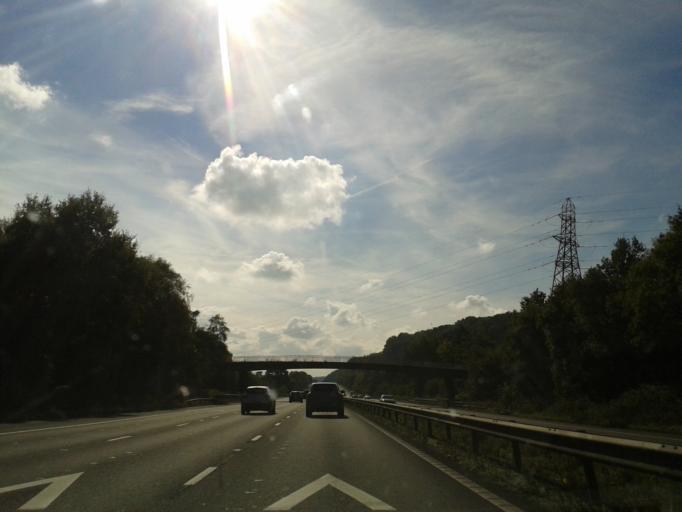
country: GB
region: England
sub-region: Staffordshire
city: Barlaston
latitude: 52.9527
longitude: -2.2185
